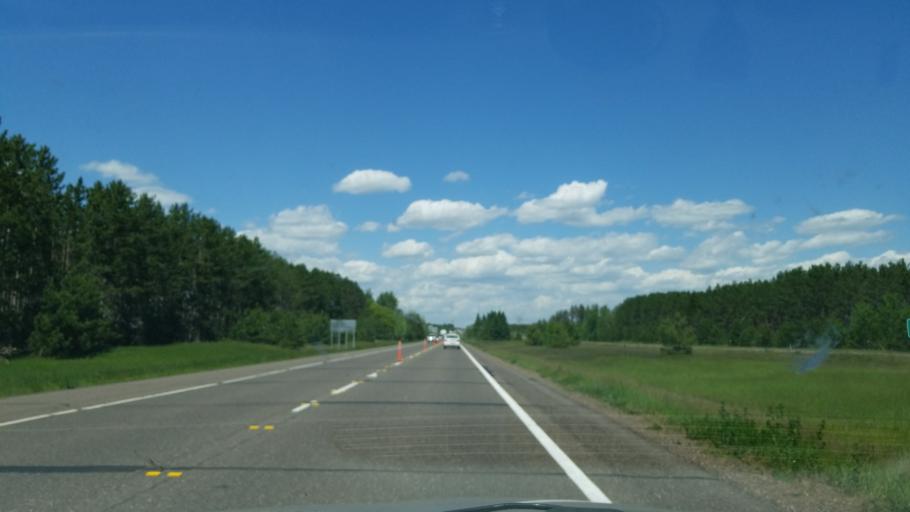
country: US
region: Minnesota
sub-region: Carlton County
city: Moose Lake
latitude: 46.3277
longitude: -92.8234
